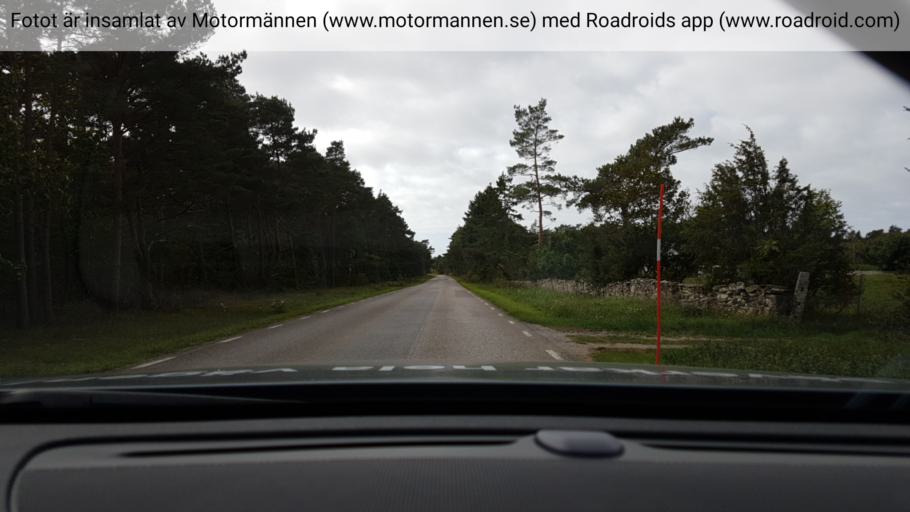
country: SE
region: Gotland
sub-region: Gotland
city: Hemse
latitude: 56.9593
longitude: 18.2191
